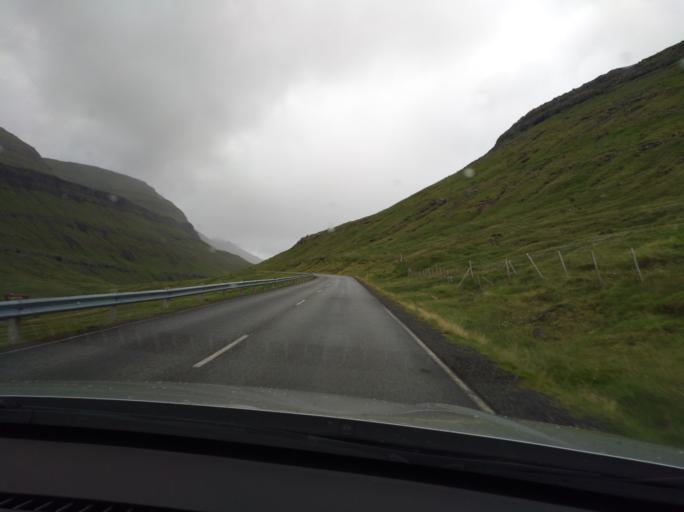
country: FO
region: Eysturoy
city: Fuglafjordur
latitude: 62.2281
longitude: -6.8790
